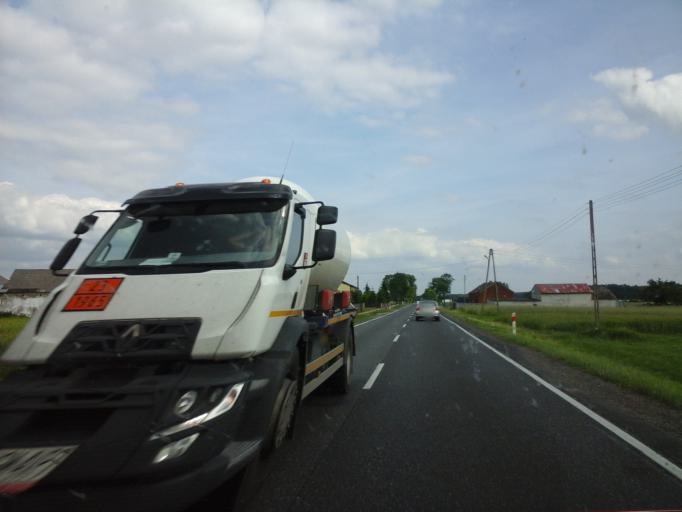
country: PL
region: Lodz Voivodeship
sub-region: Powiat opoczynski
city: Mniszkow
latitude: 51.3235
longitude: 20.0457
